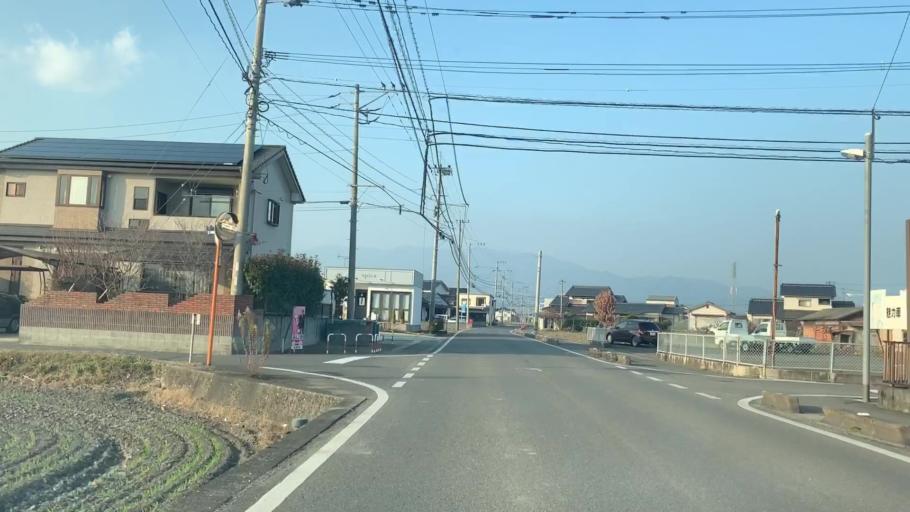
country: JP
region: Saga Prefecture
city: Saga-shi
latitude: 33.2646
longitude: 130.2310
